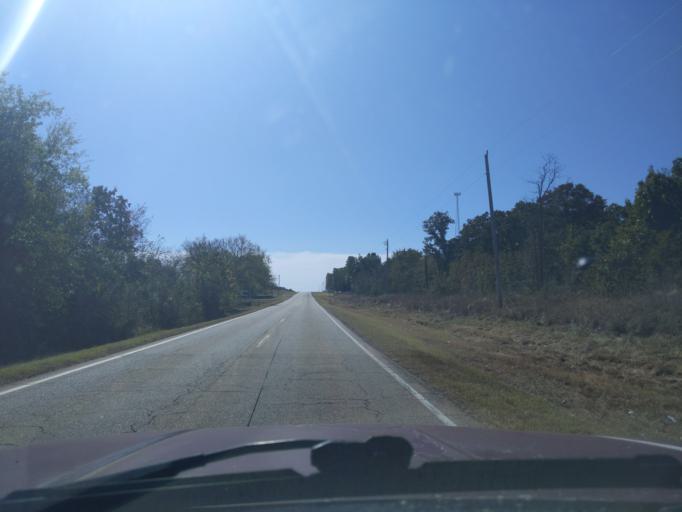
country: US
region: Oklahoma
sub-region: Creek County
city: Bristow
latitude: 35.7248
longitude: -96.3872
